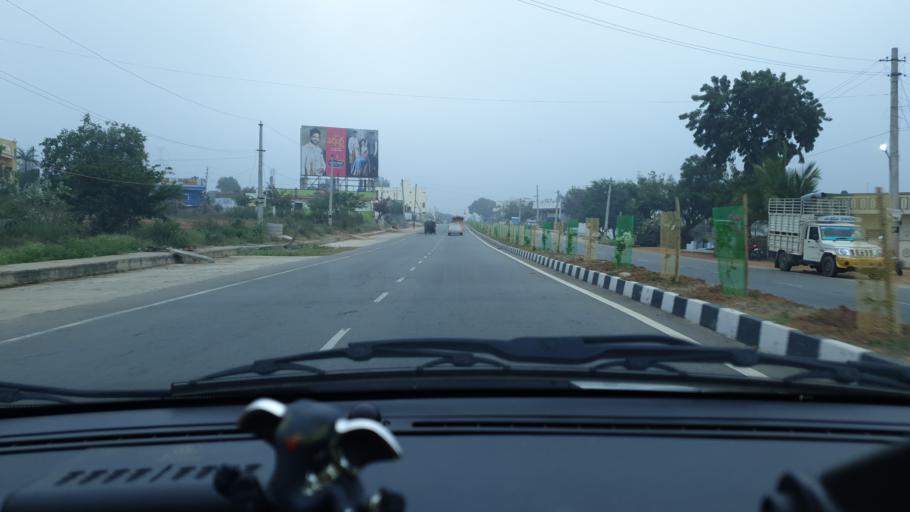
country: IN
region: Telangana
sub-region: Mahbubnagar
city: Farrukhnagar
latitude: 16.9526
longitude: 78.5198
